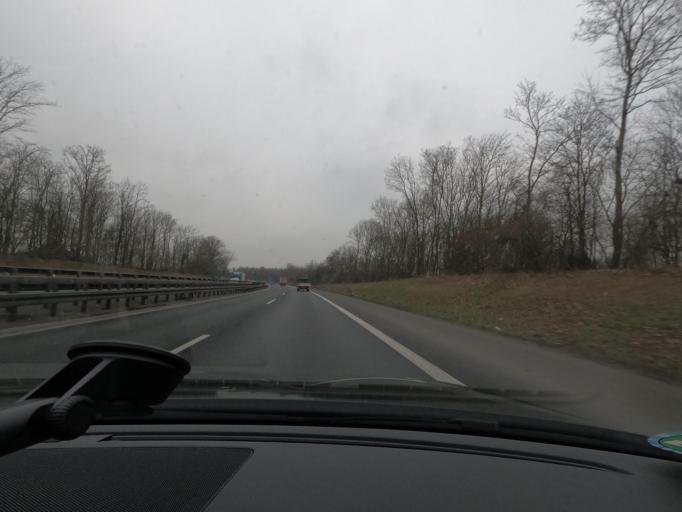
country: DE
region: North Rhine-Westphalia
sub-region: Regierungsbezirk Dusseldorf
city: Monchengladbach
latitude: 51.1300
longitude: 6.4233
